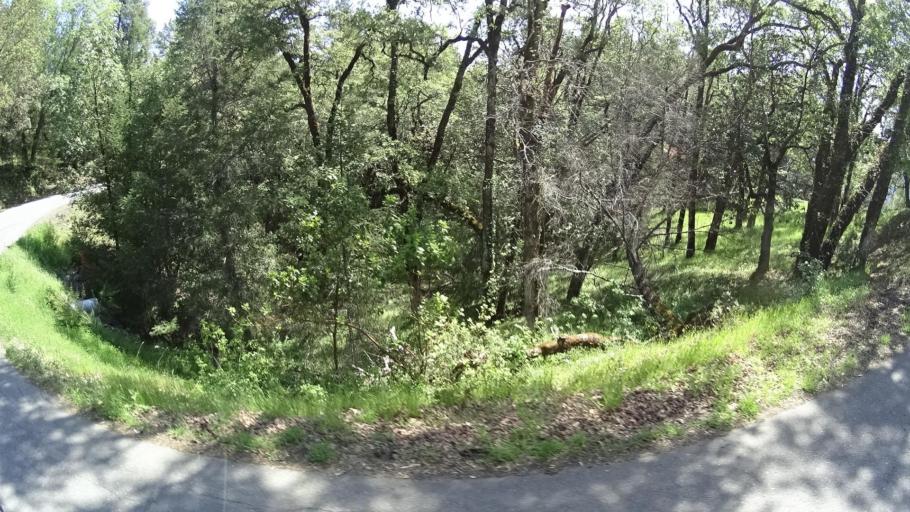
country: US
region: California
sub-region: Humboldt County
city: Redway
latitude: 40.1593
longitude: -123.6167
